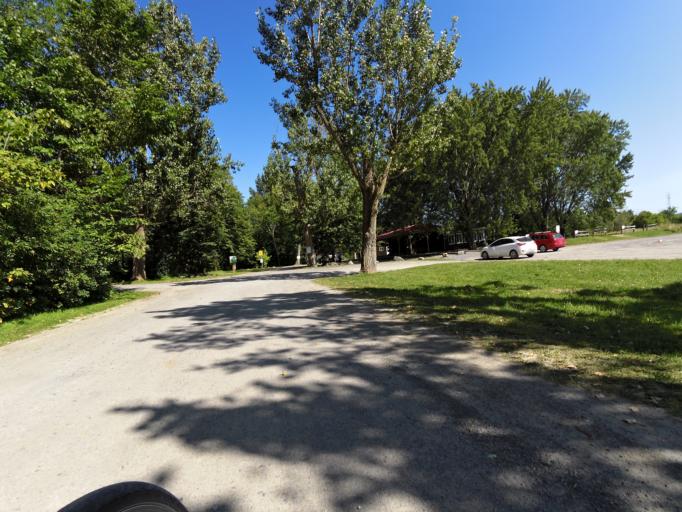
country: CA
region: Ontario
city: Bells Corners
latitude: 45.4026
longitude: -75.9225
